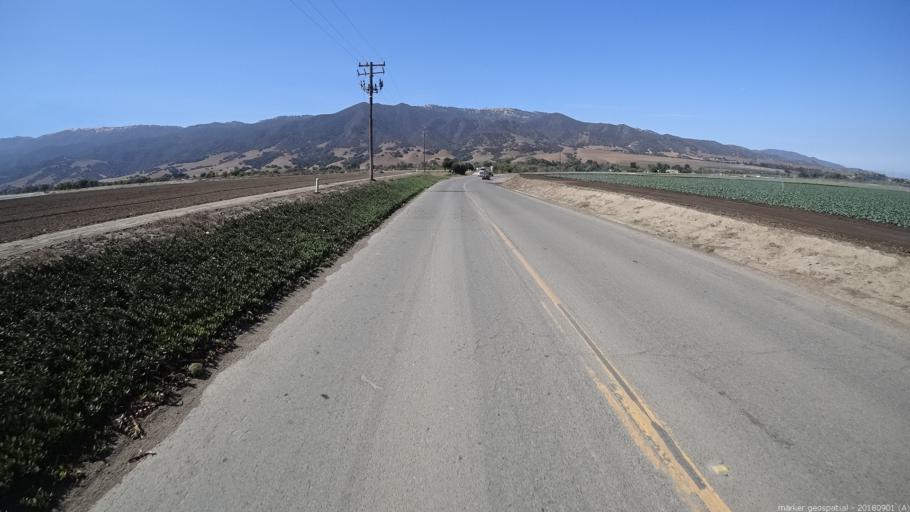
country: US
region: California
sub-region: Monterey County
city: Chualar
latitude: 36.5536
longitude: -121.5387
